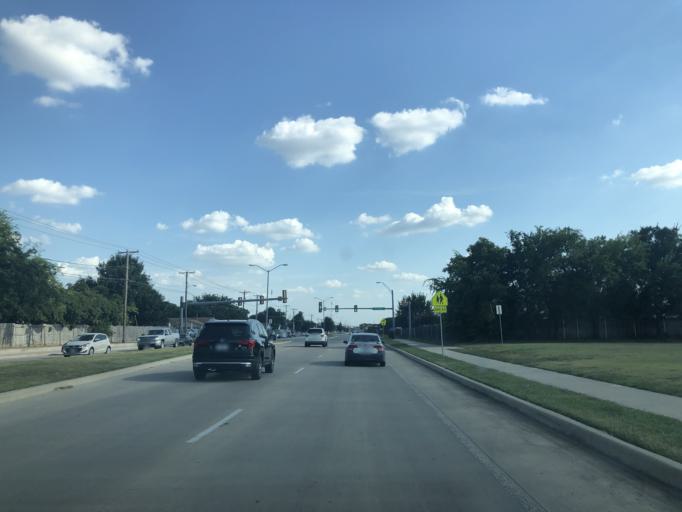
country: US
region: Texas
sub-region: Tarrant County
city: Saginaw
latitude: 32.8758
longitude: -97.3910
